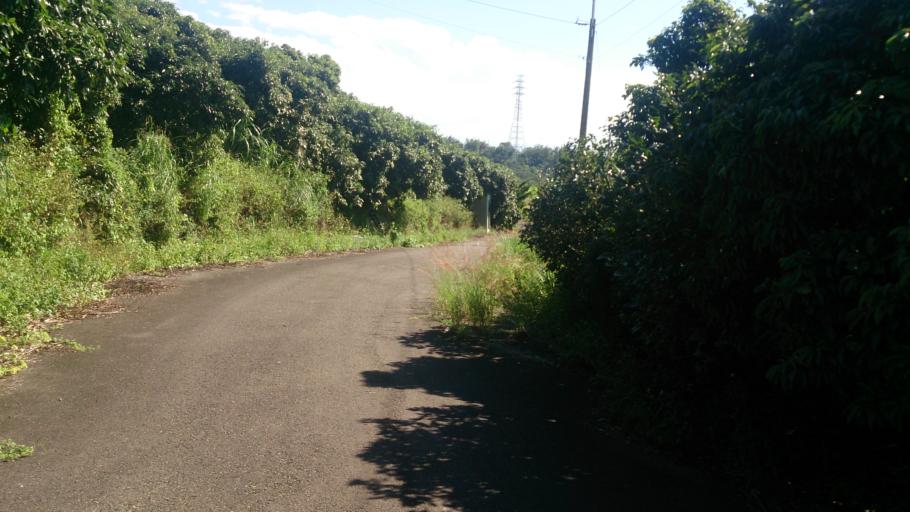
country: TW
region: Taiwan
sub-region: Hsinchu
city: Hsinchu
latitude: 24.7527
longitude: 120.9519
